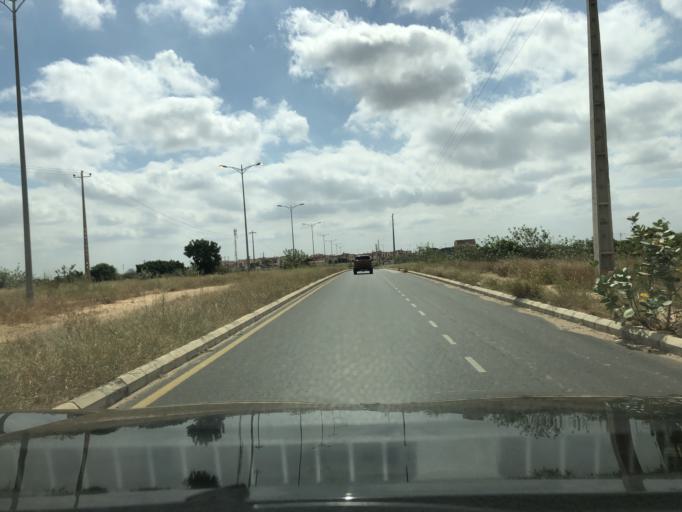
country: AO
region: Luanda
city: Luanda
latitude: -8.9570
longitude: 13.2403
